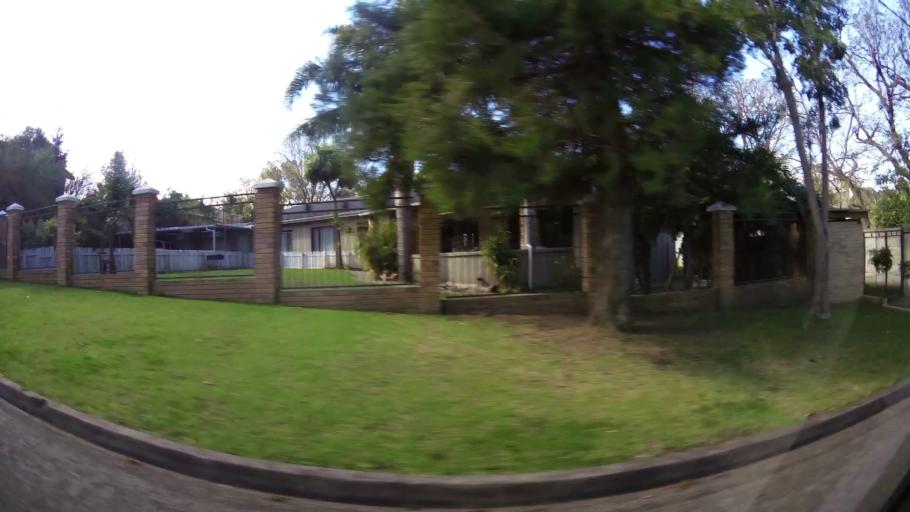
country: ZA
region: Western Cape
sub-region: Eden District Municipality
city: George
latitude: -33.9427
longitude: 22.4670
